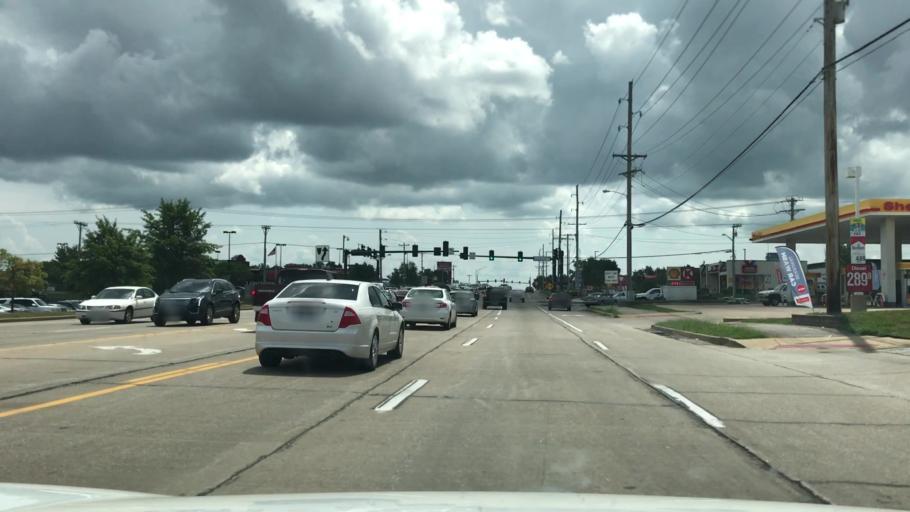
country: US
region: Missouri
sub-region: Saint Charles County
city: O'Fallon
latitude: 38.7811
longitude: -90.7000
